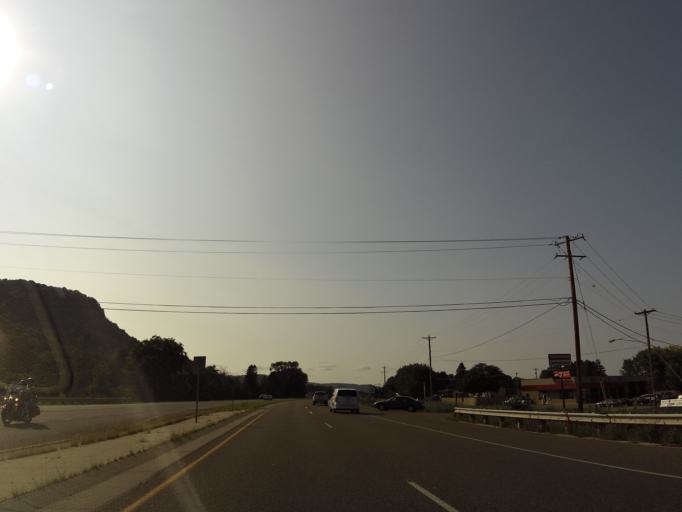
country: US
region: Minnesota
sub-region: Winona County
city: Winona
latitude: 44.0450
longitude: -91.6697
